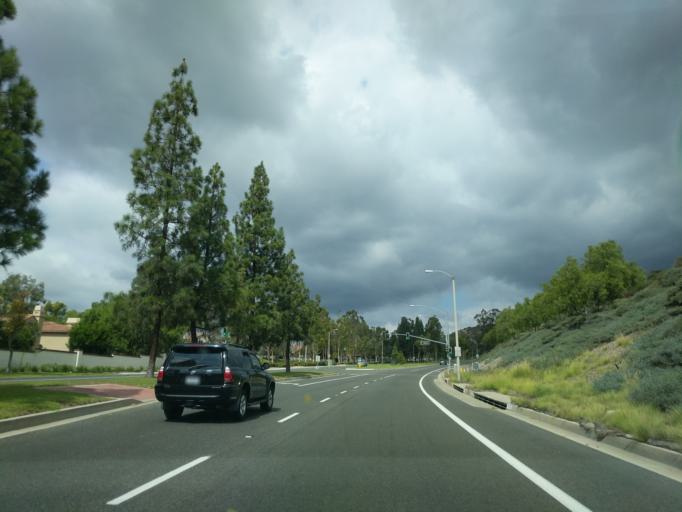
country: US
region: California
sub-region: Orange County
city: North Tustin
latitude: 33.7592
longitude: -117.7636
